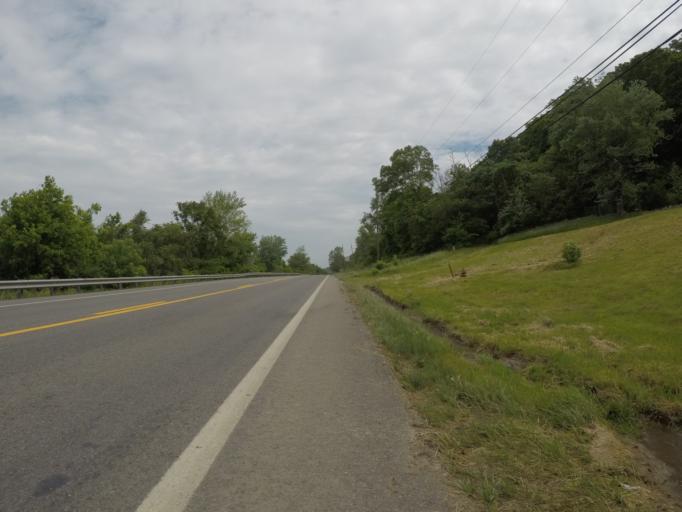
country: US
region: West Virginia
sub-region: Wayne County
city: Kenova
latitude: 38.3587
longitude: -82.5930
